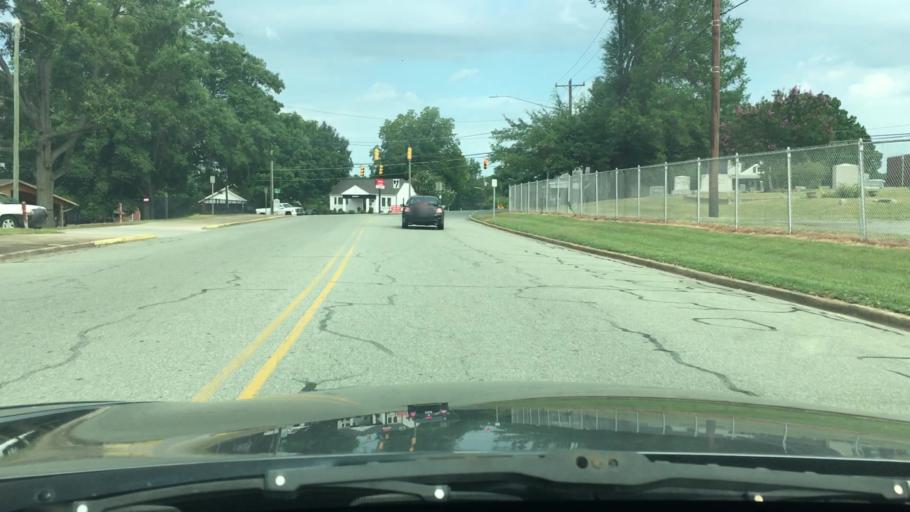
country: US
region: North Carolina
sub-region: Alamance County
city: Burlington
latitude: 36.0848
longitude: -79.4499
